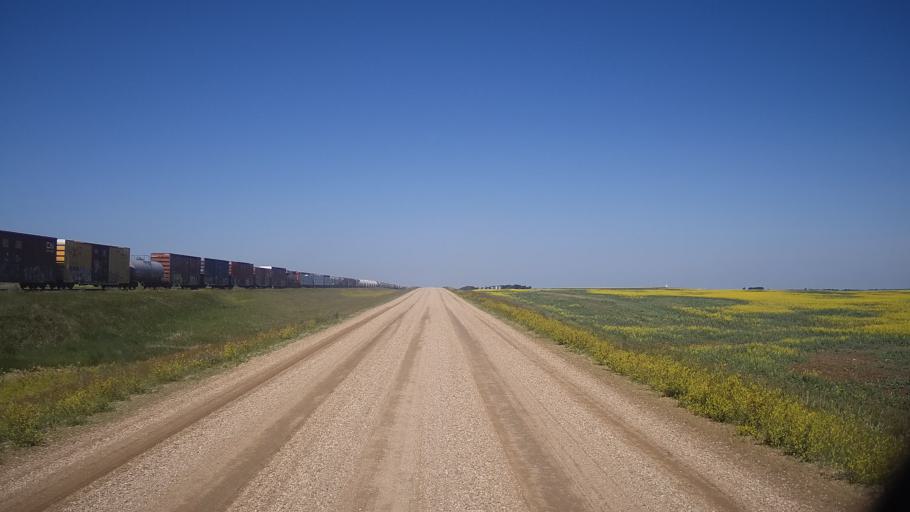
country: CA
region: Saskatchewan
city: Watrous
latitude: 51.8576
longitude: -105.9547
